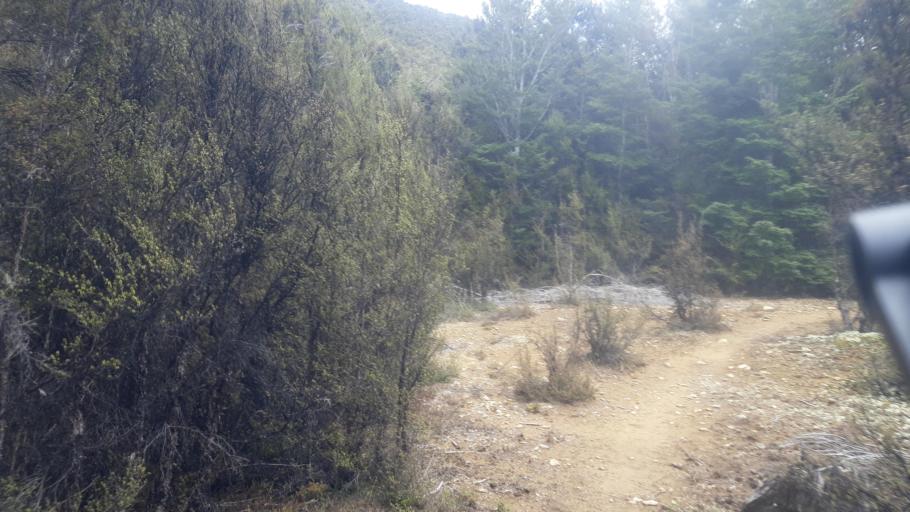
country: NZ
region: Tasman
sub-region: Tasman District
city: Wakefield
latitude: -41.7798
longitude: 172.8159
